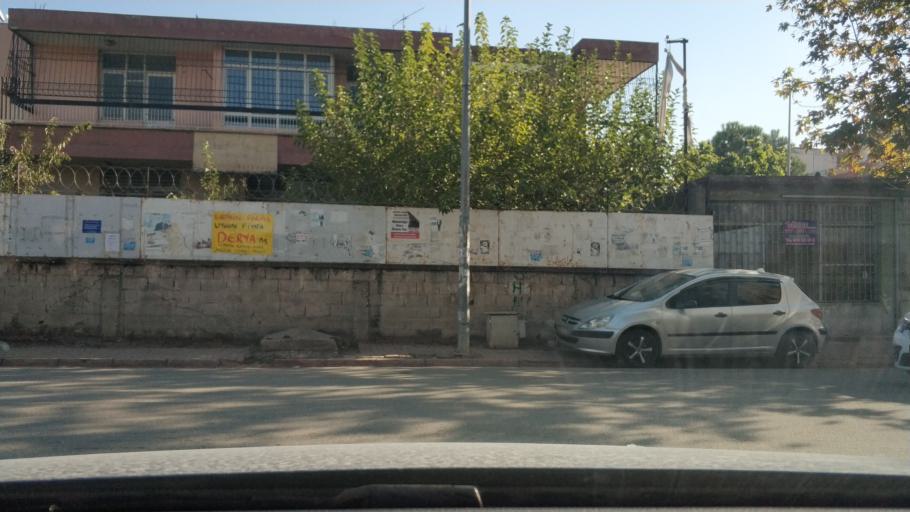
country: TR
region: Adana
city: Adana
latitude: 37.0088
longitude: 35.3154
